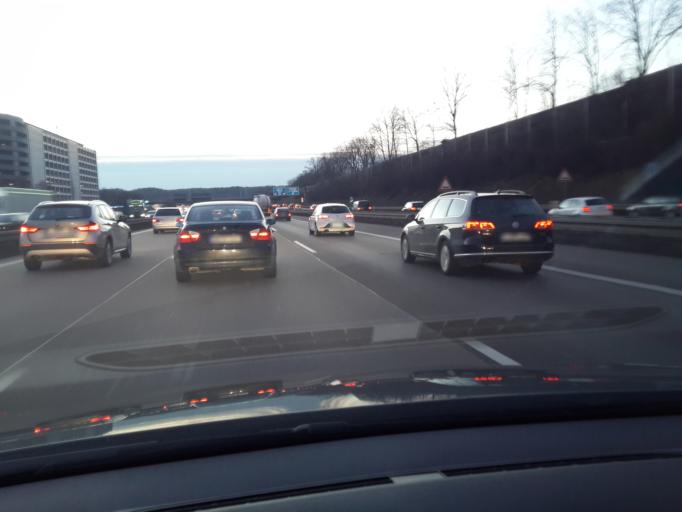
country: DE
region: Baden-Wuerttemberg
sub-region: Regierungsbezirk Stuttgart
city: Leinfelden-Echterdingen
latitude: 48.7087
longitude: 9.1481
